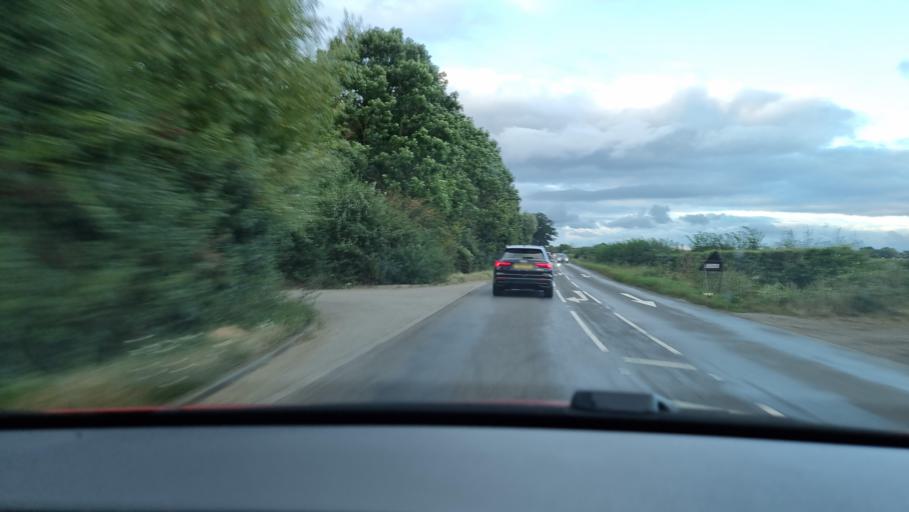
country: GB
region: England
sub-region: Milton Keynes
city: Bow Brickhill
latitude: 51.9952
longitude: -0.6990
